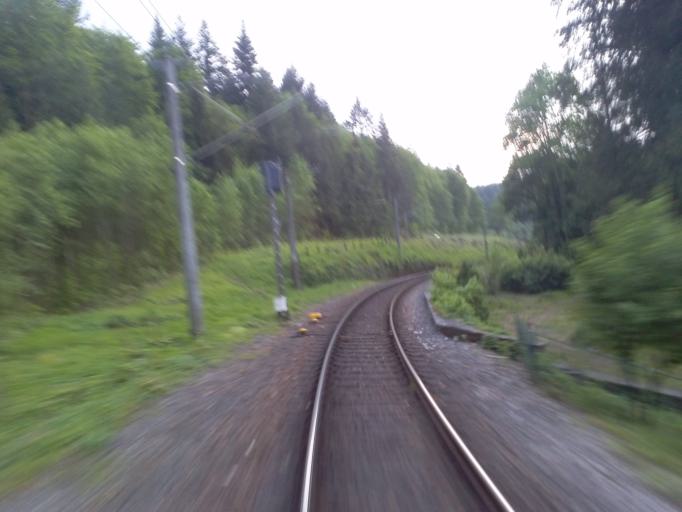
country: DE
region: Baden-Wuerttemberg
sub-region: Karlsruhe Region
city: Bad Herrenalb
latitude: 48.8602
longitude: 8.4473
